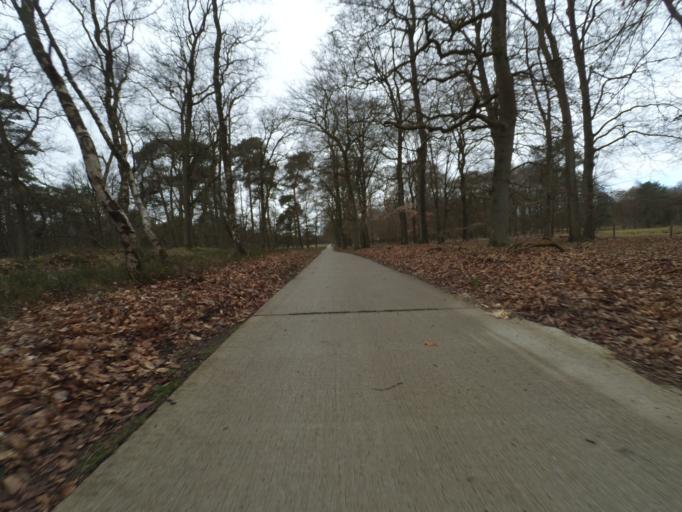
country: NL
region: Gelderland
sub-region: Gemeente Apeldoorn
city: Loenen
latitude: 52.0644
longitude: 5.9984
